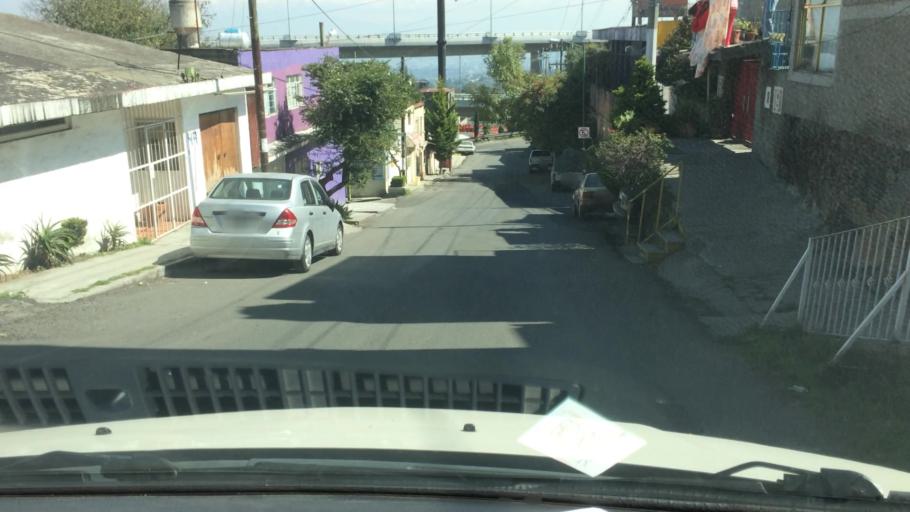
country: MX
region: Mexico City
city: Xochimilco
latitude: 19.2394
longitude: -99.1485
